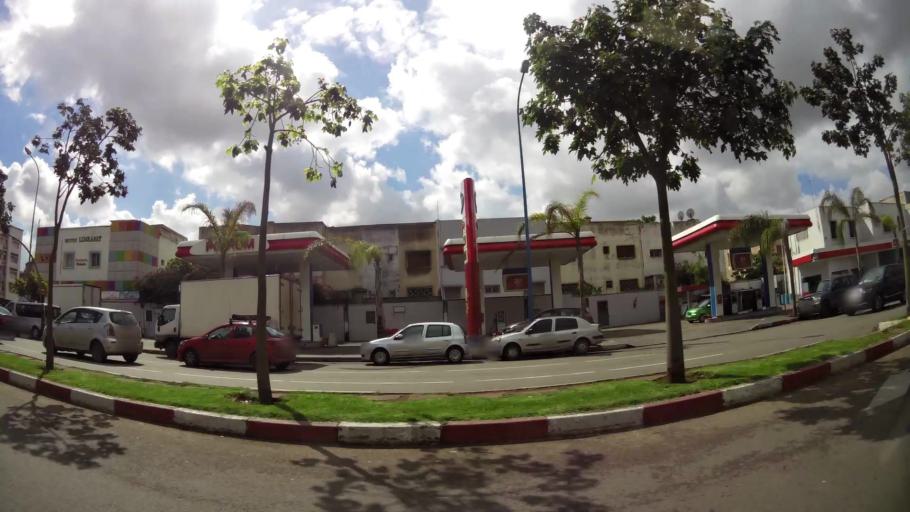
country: MA
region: Grand Casablanca
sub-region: Casablanca
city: Casablanca
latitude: 33.5532
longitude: -7.6049
